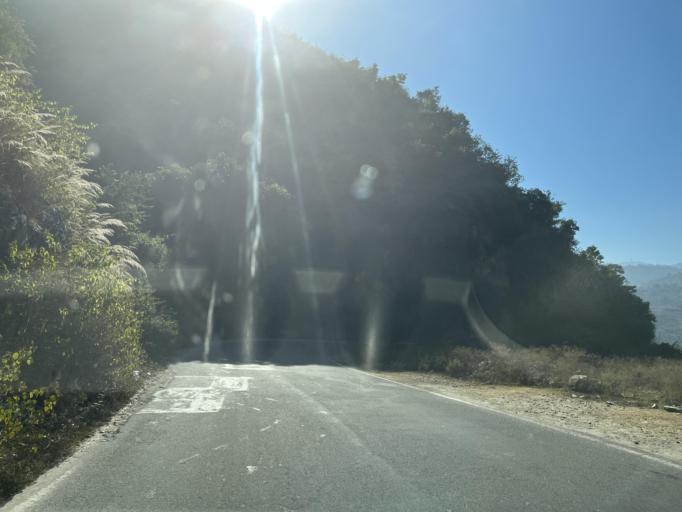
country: IN
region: Uttarakhand
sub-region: Naini Tal
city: Naini Tal
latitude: 29.5182
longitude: 79.4802
